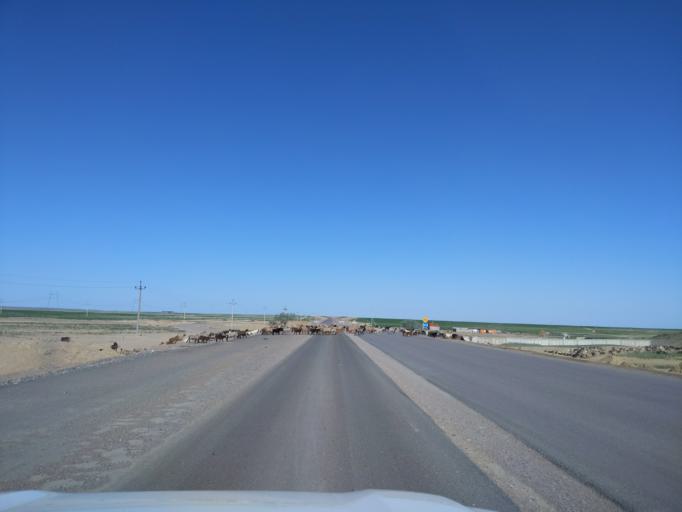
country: KZ
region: Almaty Oblysy
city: Bakanas
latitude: 44.0946
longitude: 75.9862
